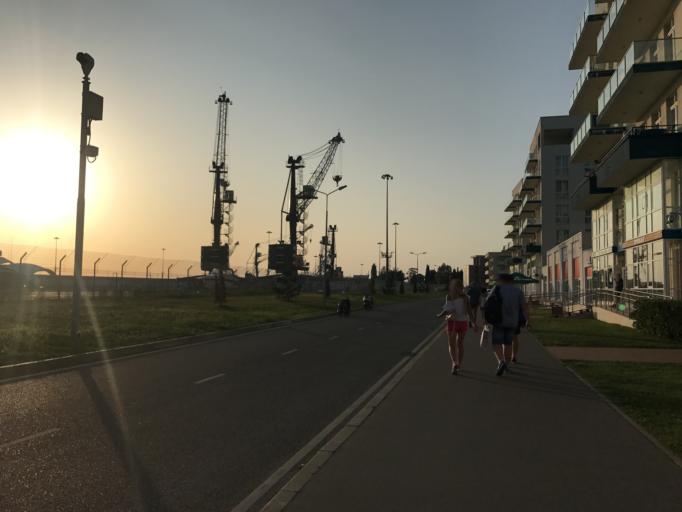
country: RU
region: Krasnodarskiy
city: Adler
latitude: 43.4122
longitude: 39.9335
